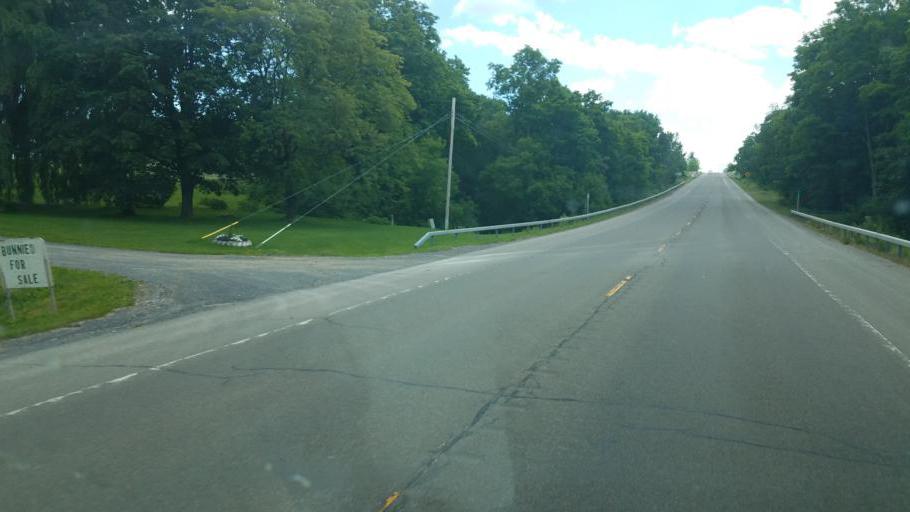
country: US
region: New York
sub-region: Yates County
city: Keuka Park
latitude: 42.5963
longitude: -77.0374
